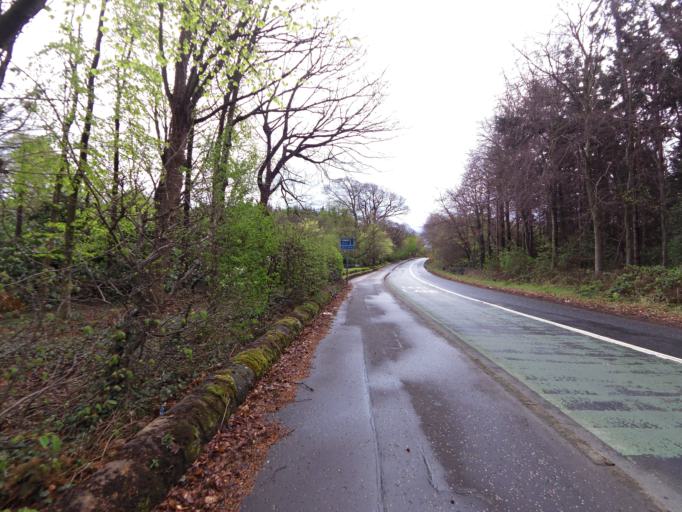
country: GB
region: Scotland
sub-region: Edinburgh
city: Ratho
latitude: 55.9713
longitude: -3.3266
